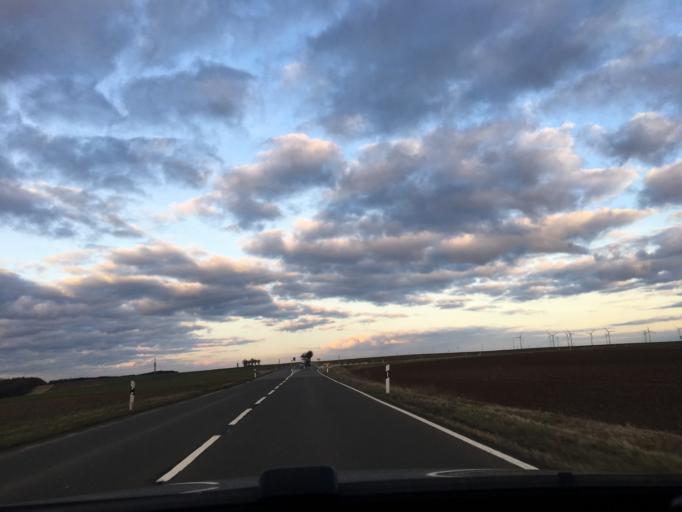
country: DE
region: Rheinland-Pfalz
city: Freimersheim
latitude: 49.7227
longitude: 8.0899
